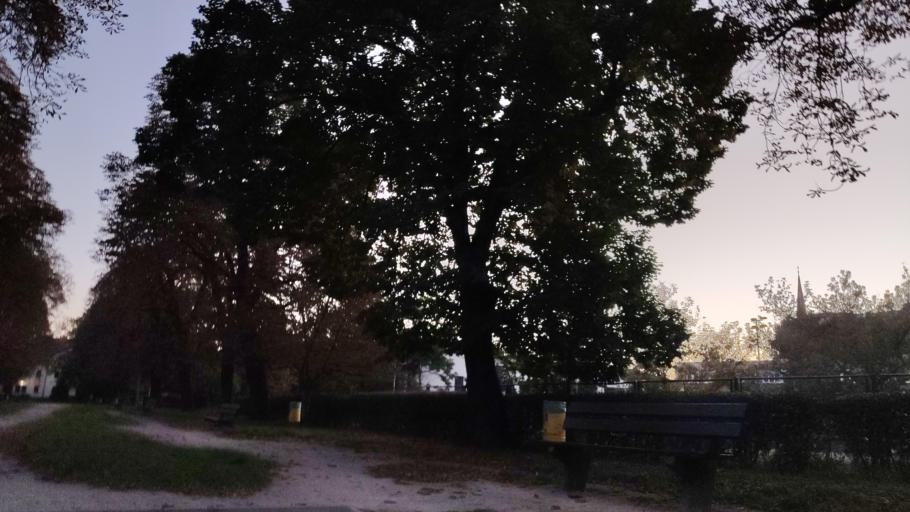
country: PL
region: Lower Silesian Voivodeship
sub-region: Powiat wroclawski
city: Wroclaw
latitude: 51.0881
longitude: 17.0226
